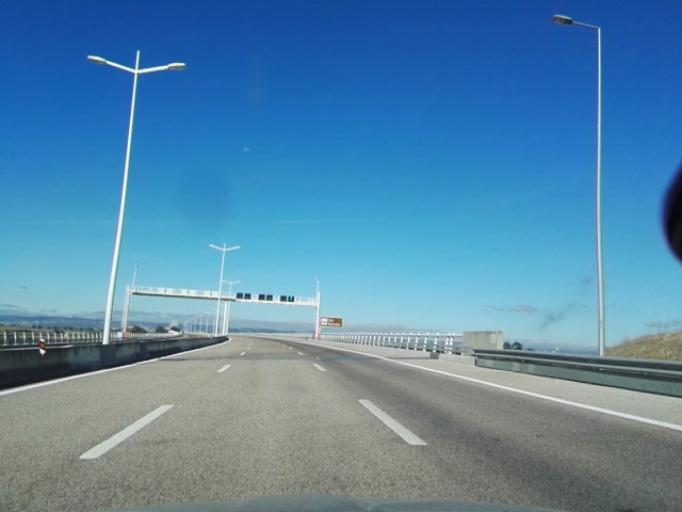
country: PT
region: Santarem
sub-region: Benavente
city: Benavente
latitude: 38.9665
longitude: -8.8446
